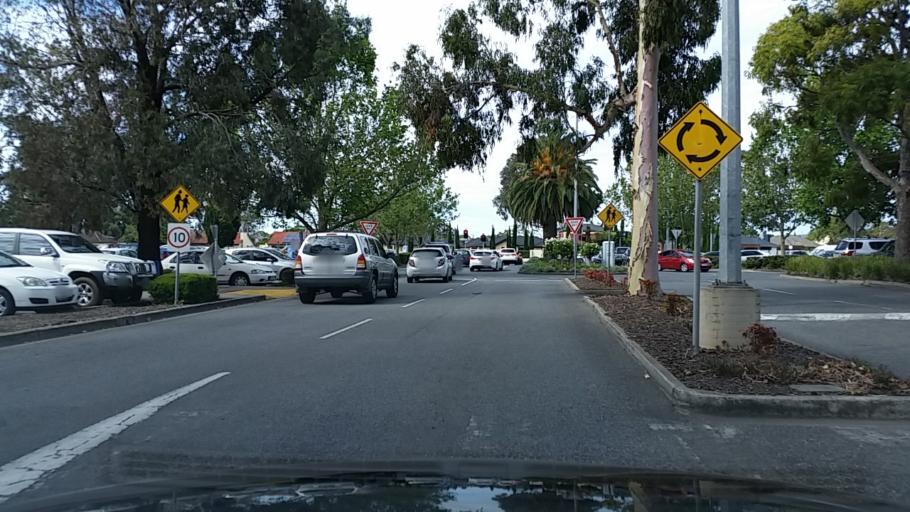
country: AU
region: South Australia
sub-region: Marion
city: Sturt
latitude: -35.0148
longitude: 138.5443
